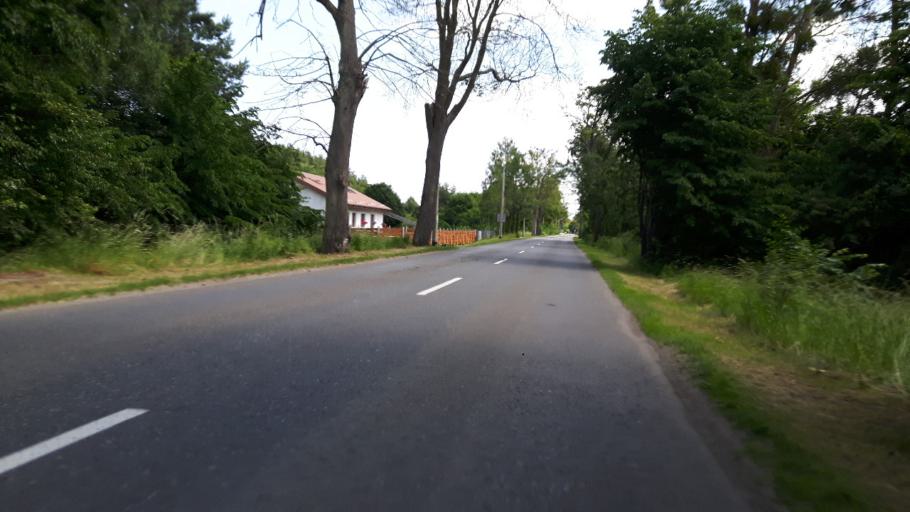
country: PL
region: Pomeranian Voivodeship
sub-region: Powiat gdanski
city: Cedry Wielkie
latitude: 54.3388
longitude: 18.8985
